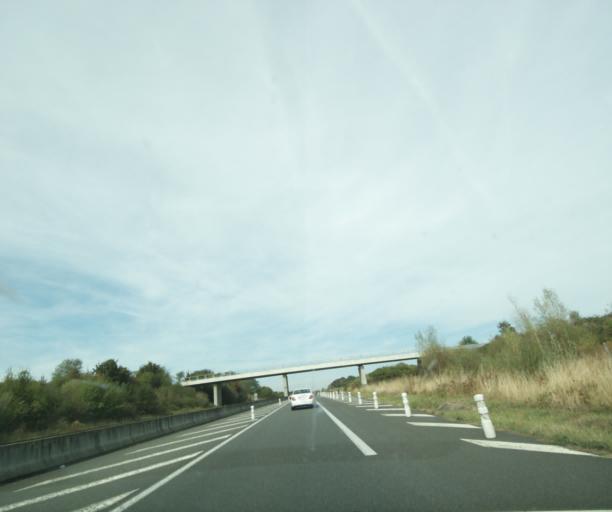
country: FR
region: Auvergne
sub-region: Departement de l'Allier
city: Lapalisse
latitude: 46.2411
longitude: 3.6198
